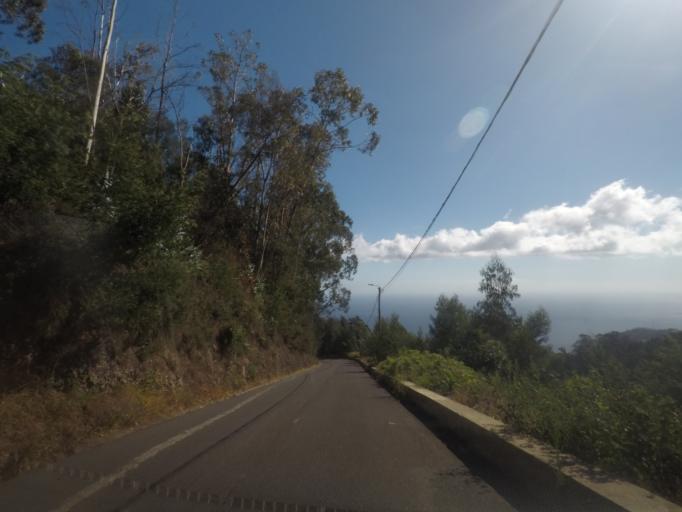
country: PT
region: Madeira
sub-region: Ribeira Brava
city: Campanario
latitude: 32.6840
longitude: -17.0233
